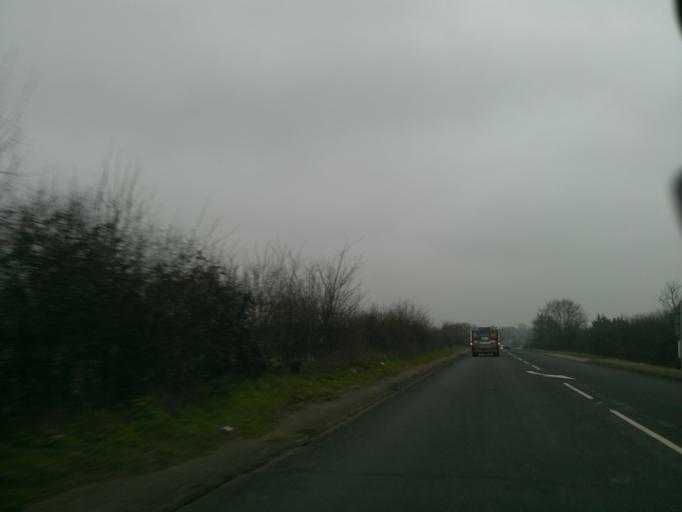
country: GB
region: England
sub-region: Essex
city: Alresford
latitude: 51.8748
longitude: 1.0090
